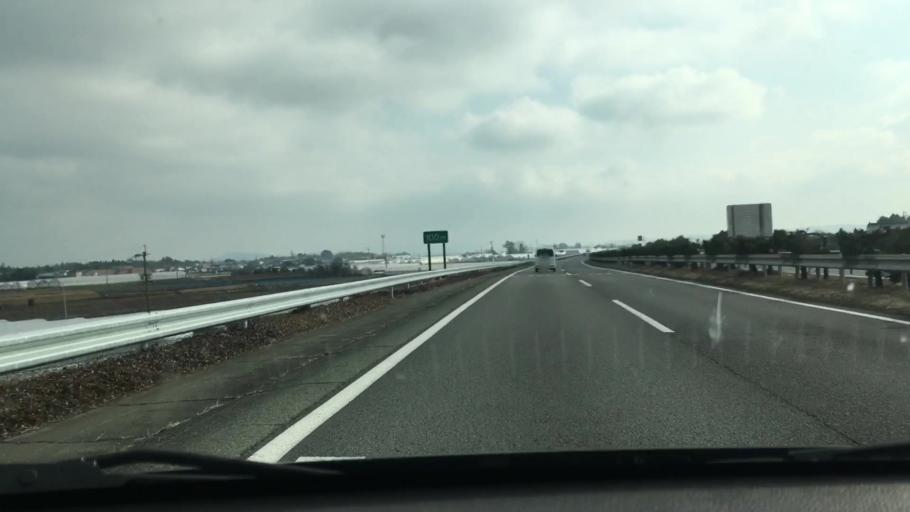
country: JP
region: Kumamoto
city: Ueki
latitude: 32.8869
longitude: 130.7244
